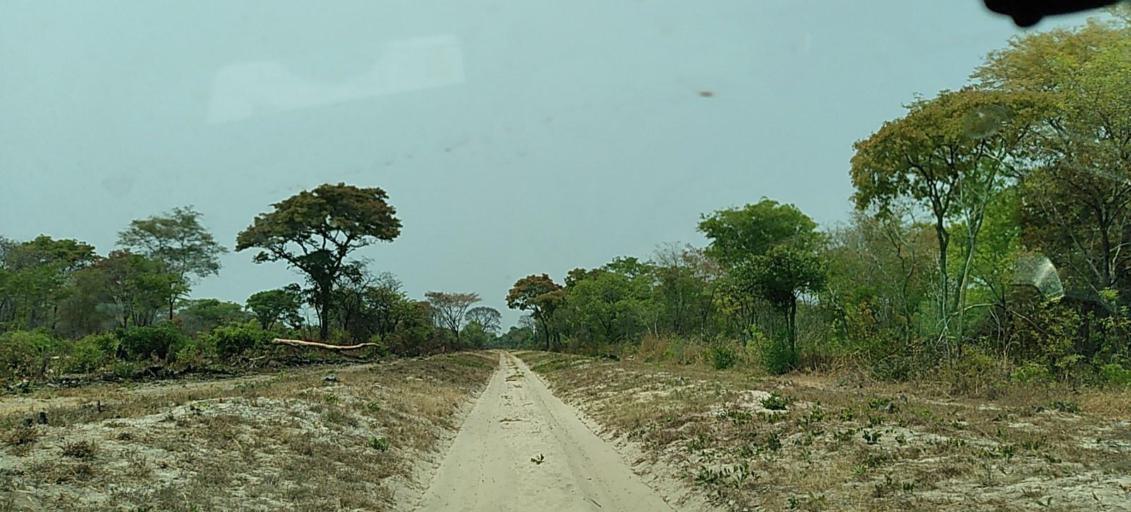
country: ZM
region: Western
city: Lukulu
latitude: -14.1444
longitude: 23.2867
